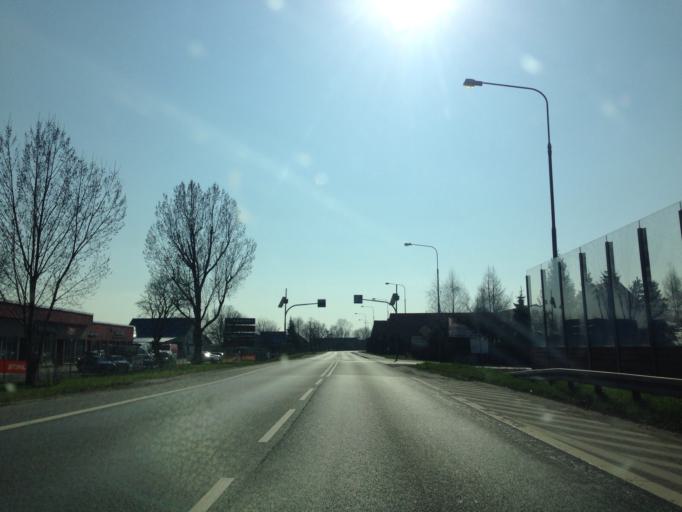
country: PL
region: Lower Silesian Voivodeship
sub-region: Powiat olesnicki
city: Olesnica
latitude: 51.2036
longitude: 17.3329
